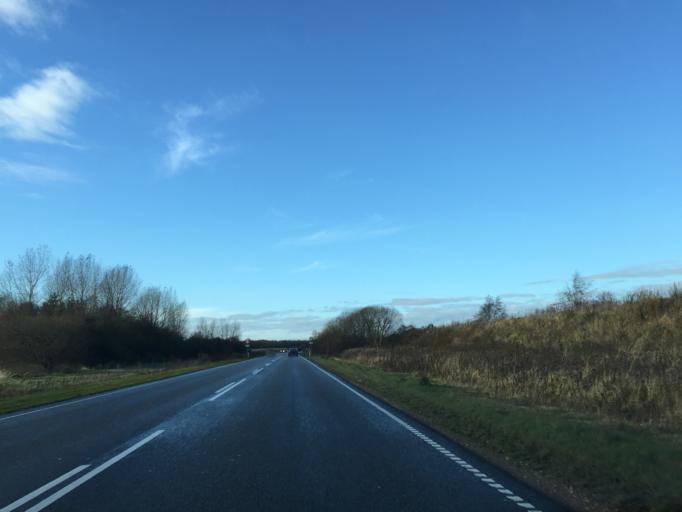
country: DK
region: Central Jutland
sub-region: Arhus Kommune
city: Sabro
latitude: 56.1987
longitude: 10.0572
